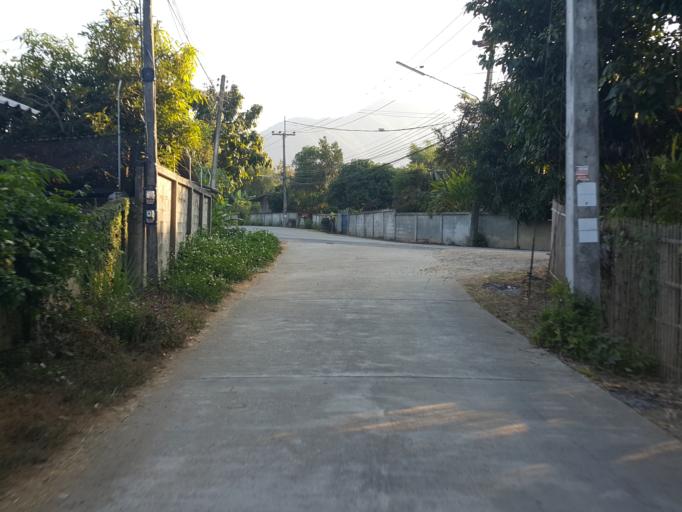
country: TH
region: Chiang Mai
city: Mae On
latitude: 18.7532
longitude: 99.2533
